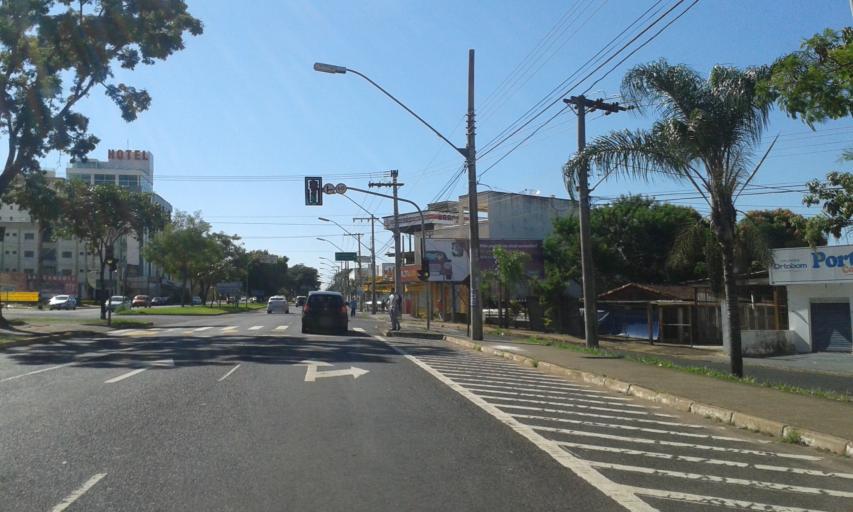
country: BR
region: Minas Gerais
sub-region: Uberlandia
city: Uberlandia
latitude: -18.9266
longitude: -48.2584
